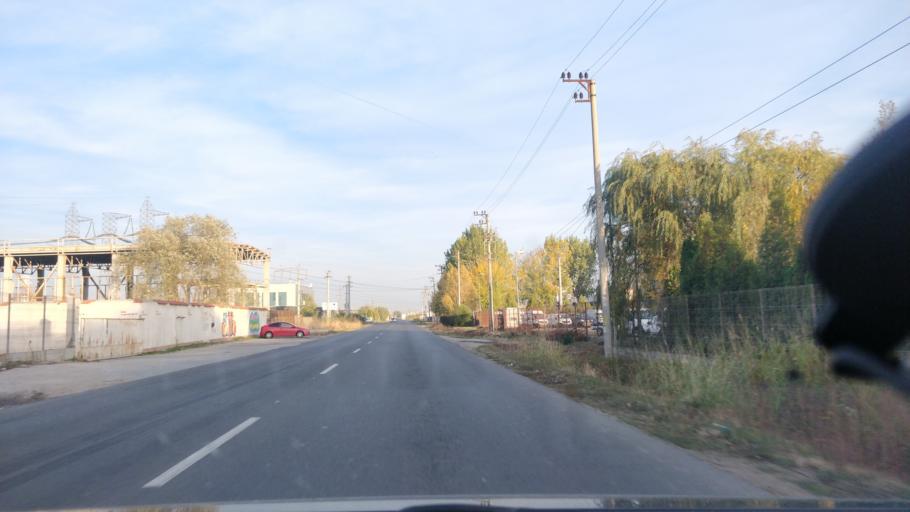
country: RO
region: Ilfov
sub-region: Comuna Ciorogarla
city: Ciorogarla
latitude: 44.4408
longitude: 25.9139
